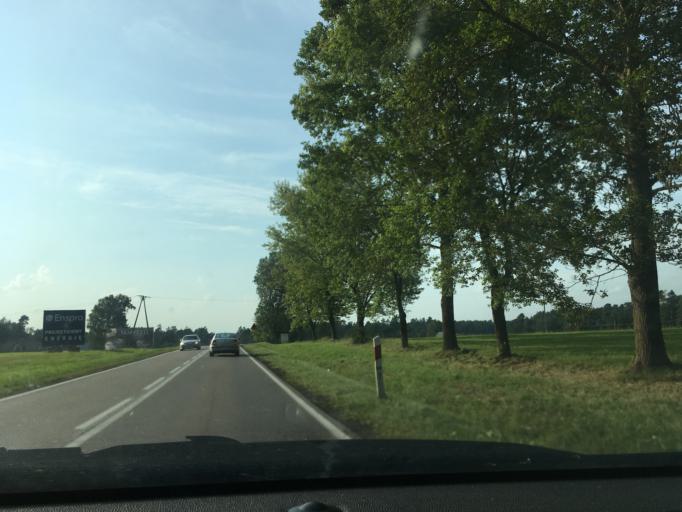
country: PL
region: Podlasie
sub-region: Powiat bialostocki
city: Dobrzyniewo Duze
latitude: 53.2560
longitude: 22.9804
